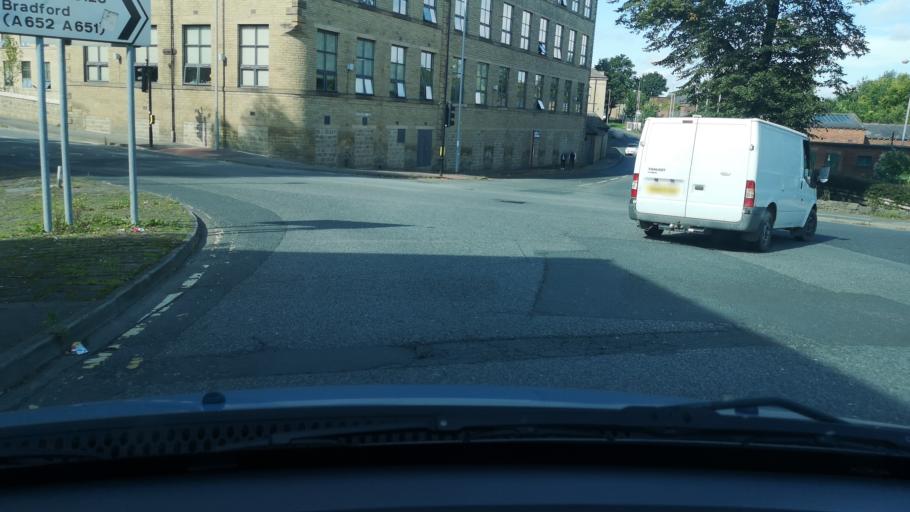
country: GB
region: England
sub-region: Kirklees
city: Batley
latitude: 53.7150
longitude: -1.6372
